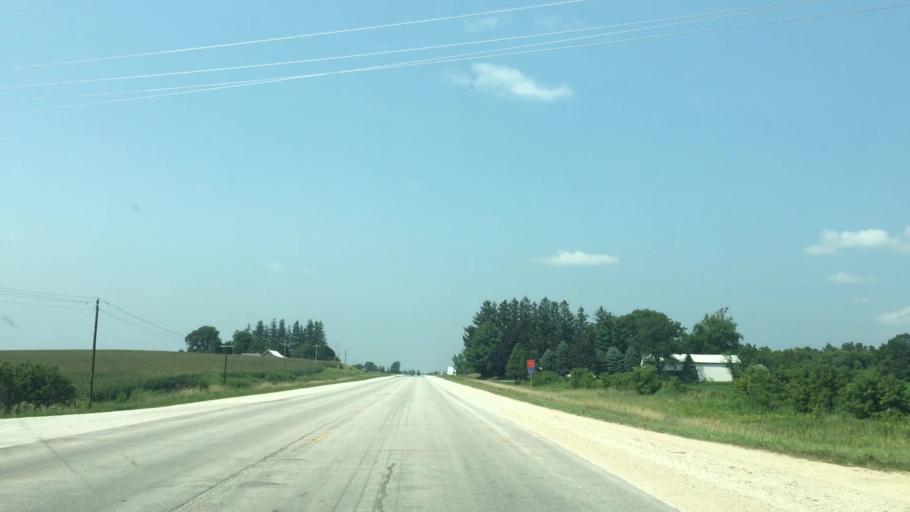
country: US
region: Iowa
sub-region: Winneshiek County
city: Decorah
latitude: 43.4286
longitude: -91.8595
